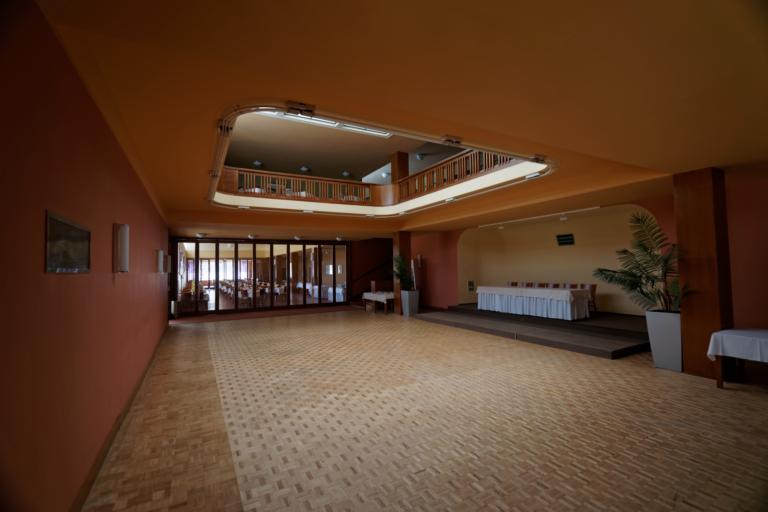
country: CZ
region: Zlin
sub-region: Okres Zlin
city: Luhacovice
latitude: 49.1075
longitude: 17.7616
